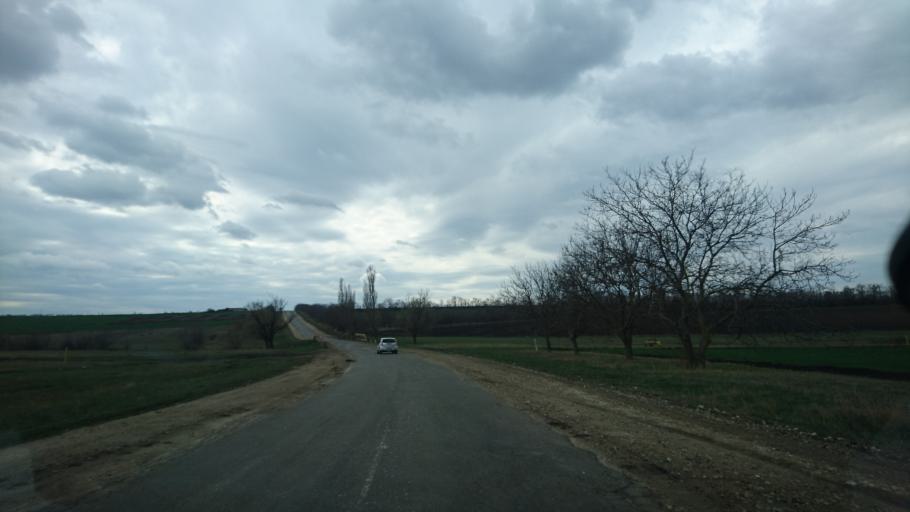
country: MD
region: Gagauzia
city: Comrat
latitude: 46.3111
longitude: 28.5860
